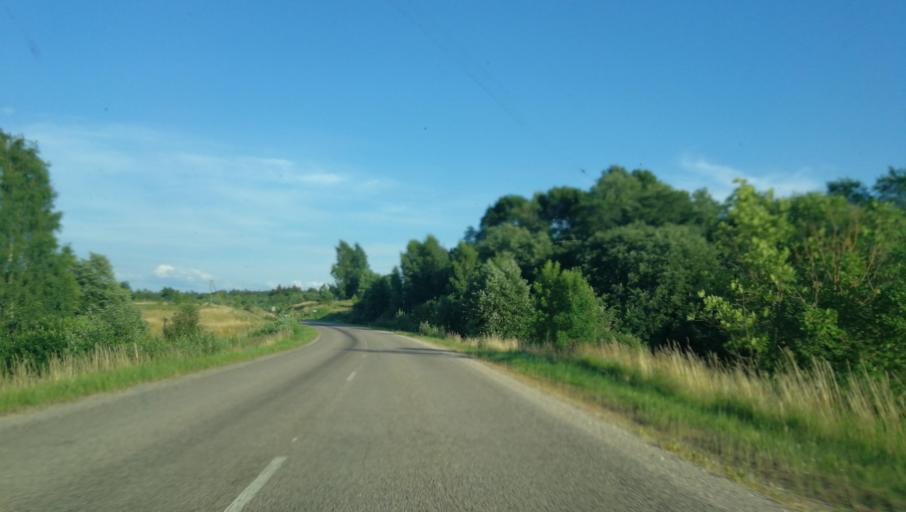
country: LV
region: Priekuli
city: Priekuli
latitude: 57.2615
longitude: 25.3580
